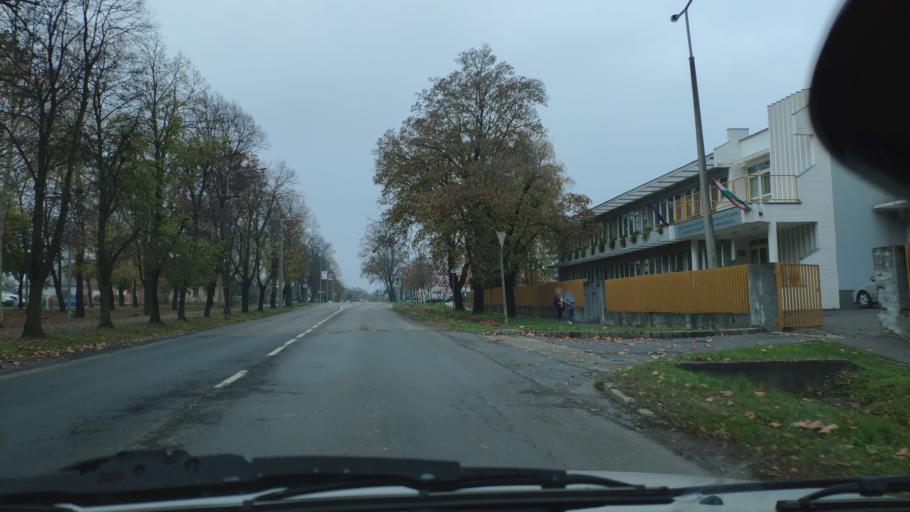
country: HU
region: Zala
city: Nagykanizsa
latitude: 46.4522
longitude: 17.0125
